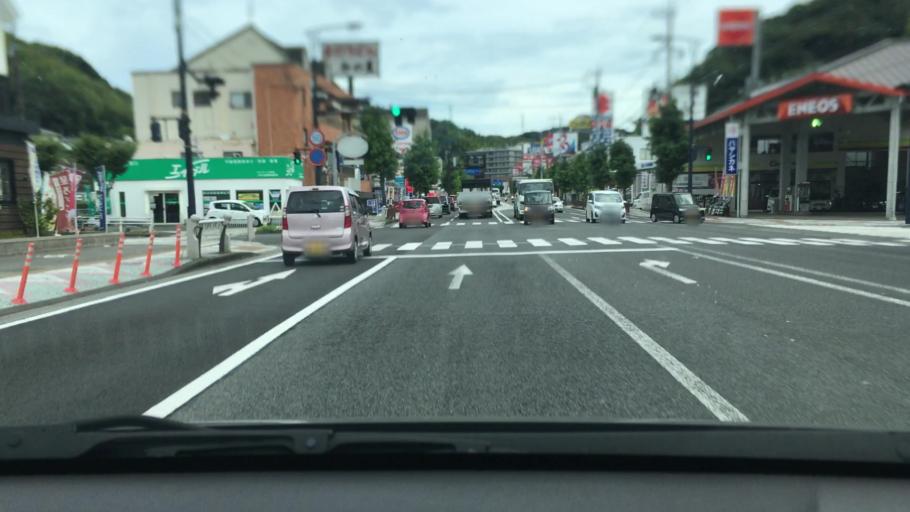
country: JP
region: Nagasaki
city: Togitsu
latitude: 32.8262
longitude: 129.8482
